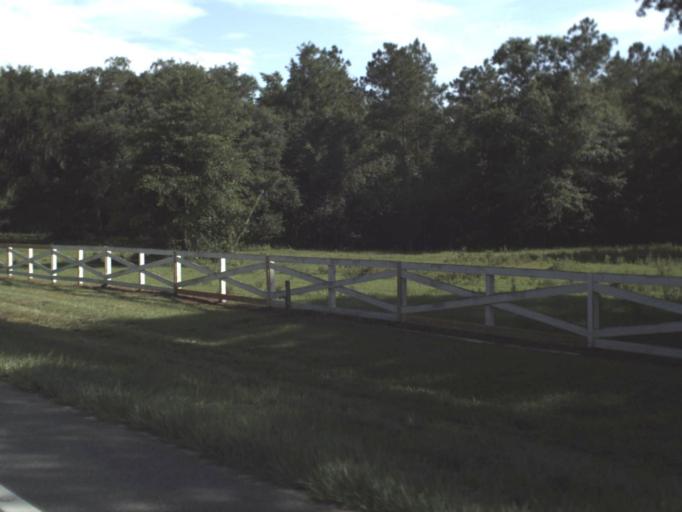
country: US
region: Florida
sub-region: Madison County
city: Madison
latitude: 30.4345
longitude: -83.3912
